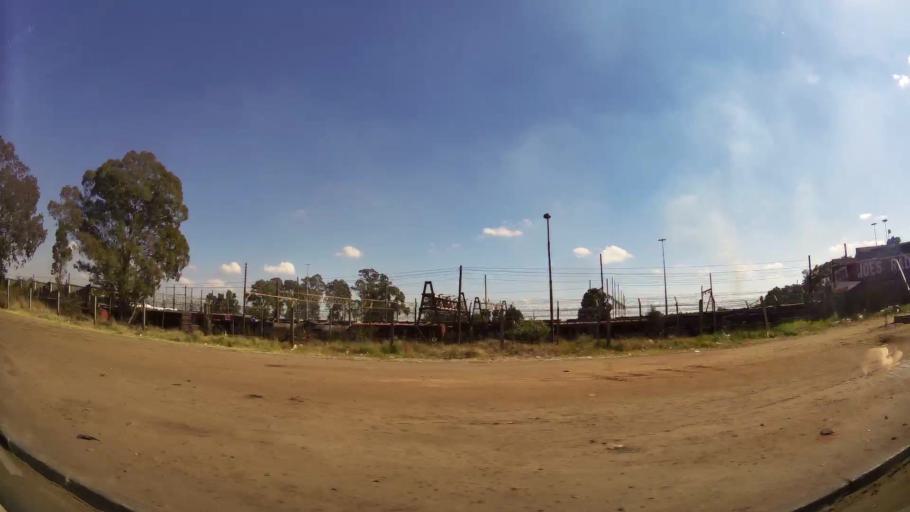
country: ZA
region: Mpumalanga
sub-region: Nkangala District Municipality
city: Witbank
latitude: -25.8742
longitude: 29.2075
